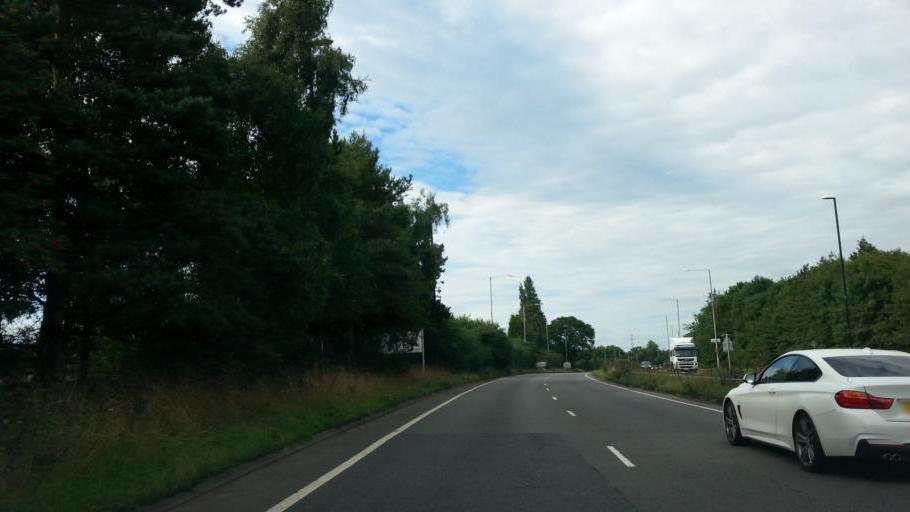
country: GB
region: England
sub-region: Warwickshire
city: Exhall
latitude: 52.4505
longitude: -1.5001
